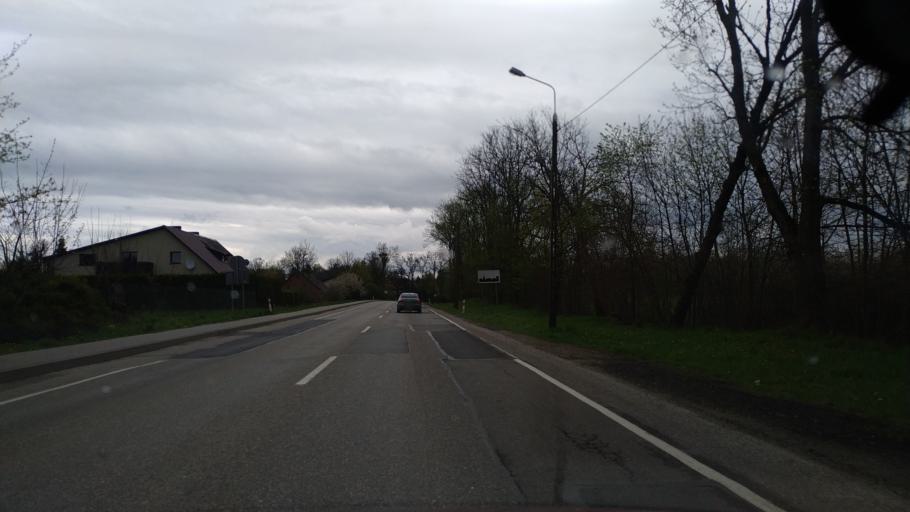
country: PL
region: Pomeranian Voivodeship
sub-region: Powiat tczewski
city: Pelplin
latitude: 54.0354
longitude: 18.6569
